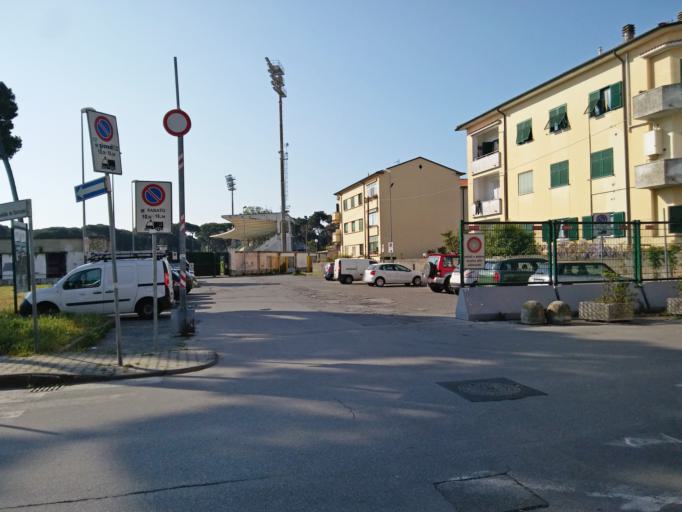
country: IT
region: Tuscany
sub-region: Provincia di Lucca
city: Viareggio
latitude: 43.8618
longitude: 10.2489
